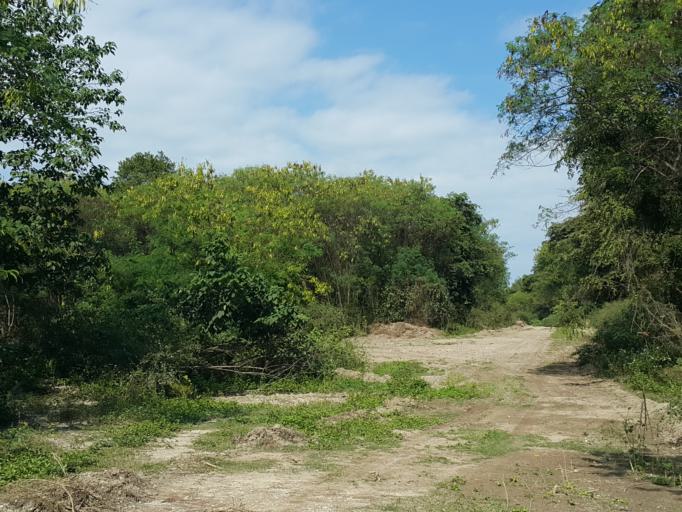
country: TH
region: Lampang
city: Mae Mo
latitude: 18.3339
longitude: 99.7674
